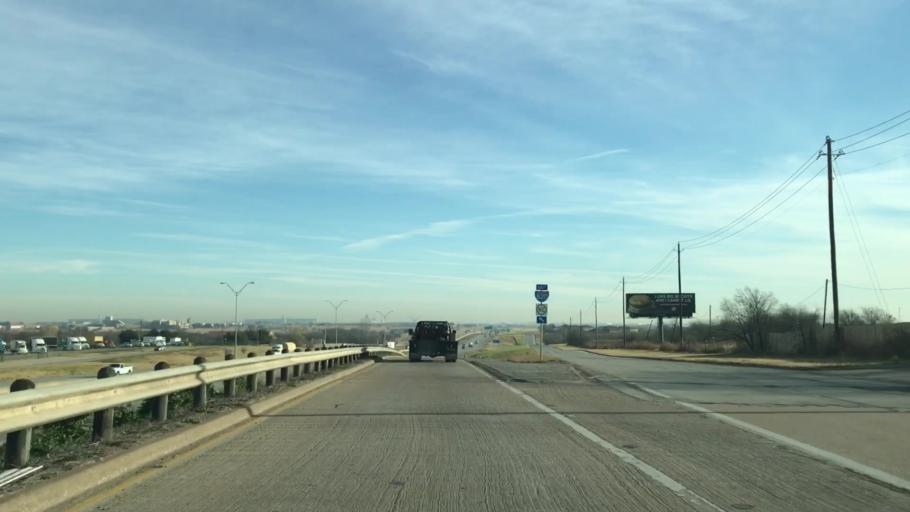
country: US
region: Texas
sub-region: Tarrant County
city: Sansom Park
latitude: 32.8156
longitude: -97.4081
